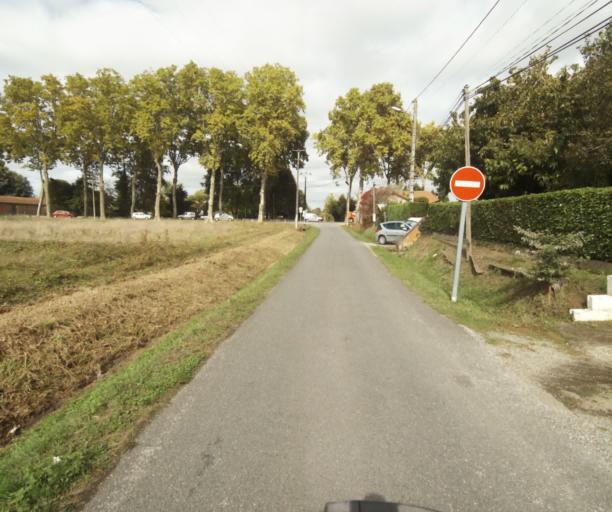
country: FR
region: Midi-Pyrenees
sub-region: Departement du Tarn-et-Garonne
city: Montech
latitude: 43.9552
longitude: 1.2235
